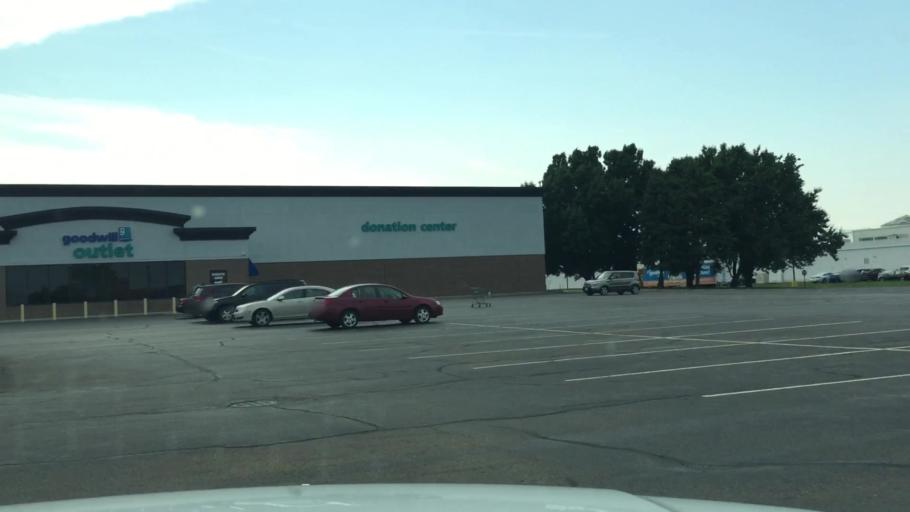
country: US
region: Ohio
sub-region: Franklin County
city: Reynoldsburg
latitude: 39.9269
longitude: -82.8343
